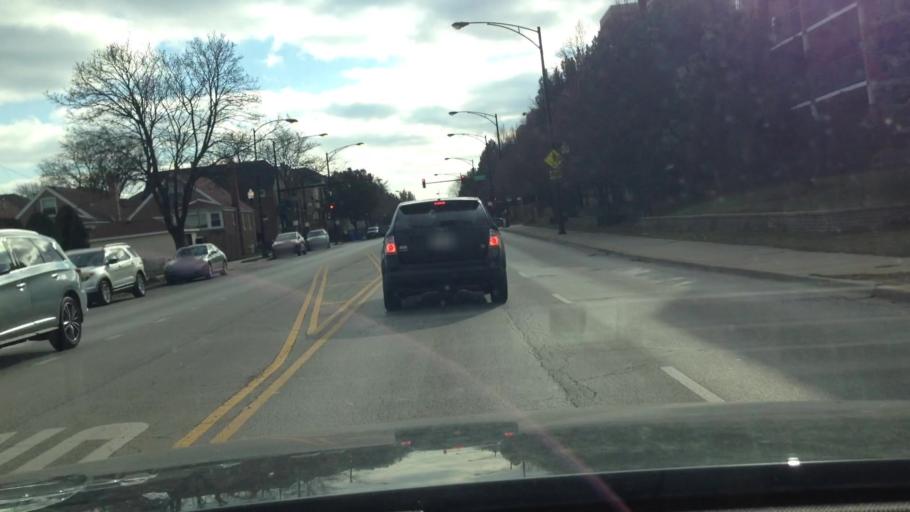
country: US
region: Illinois
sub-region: Cook County
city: Harwood Heights
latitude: 41.9575
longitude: -87.7868
